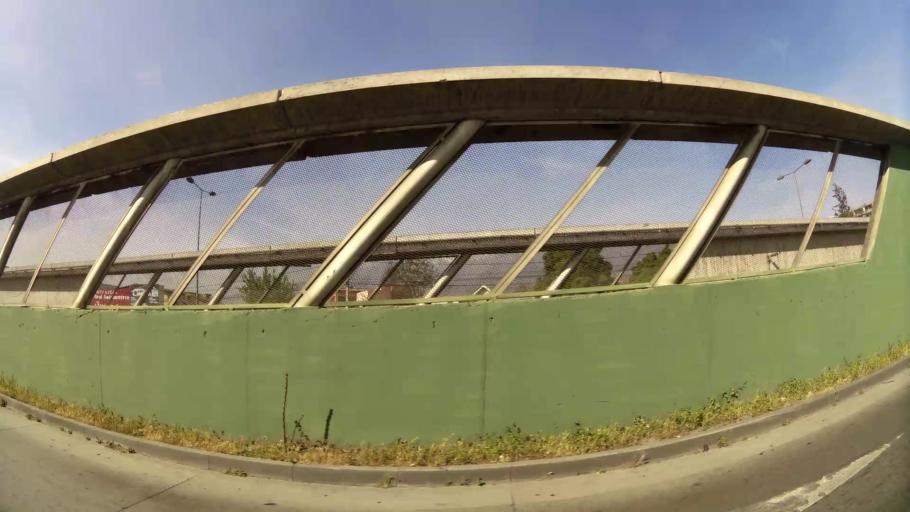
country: CL
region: Santiago Metropolitan
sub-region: Provincia de Santiago
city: La Pintana
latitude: -33.5321
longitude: -70.5946
